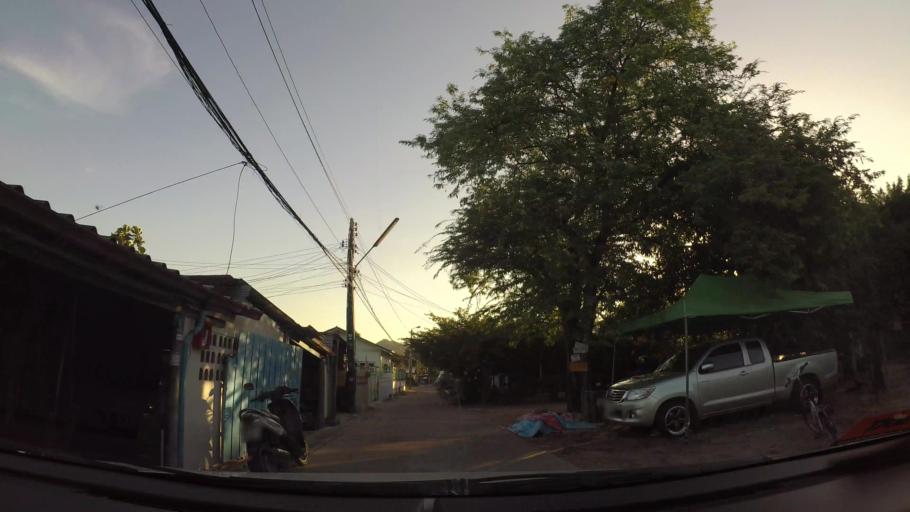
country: TH
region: Chon Buri
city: Si Racha
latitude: 13.1321
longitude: 100.9394
